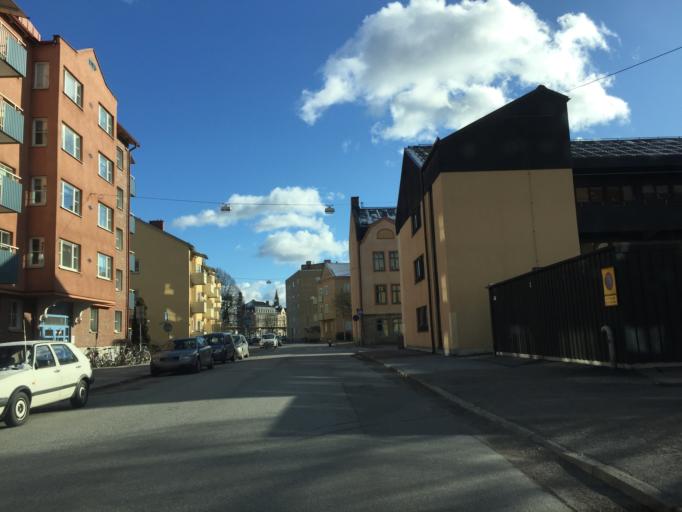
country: SE
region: OErebro
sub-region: Orebro Kommun
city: Orebro
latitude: 59.2794
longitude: 15.2095
